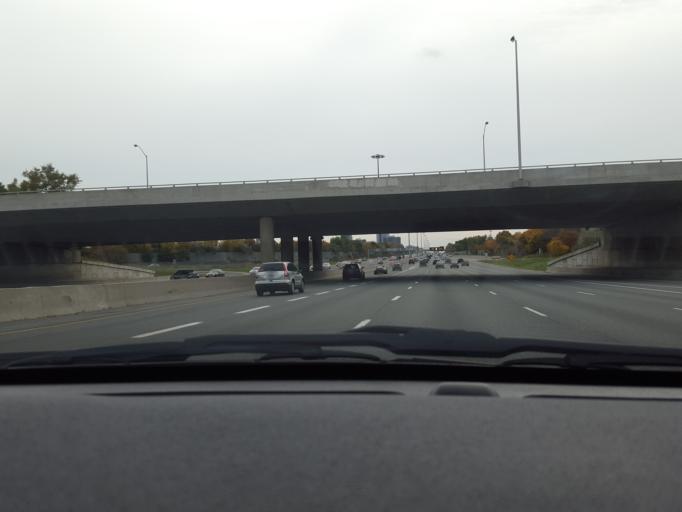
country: CA
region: Ontario
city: Willowdale
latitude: 43.7958
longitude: -79.3440
